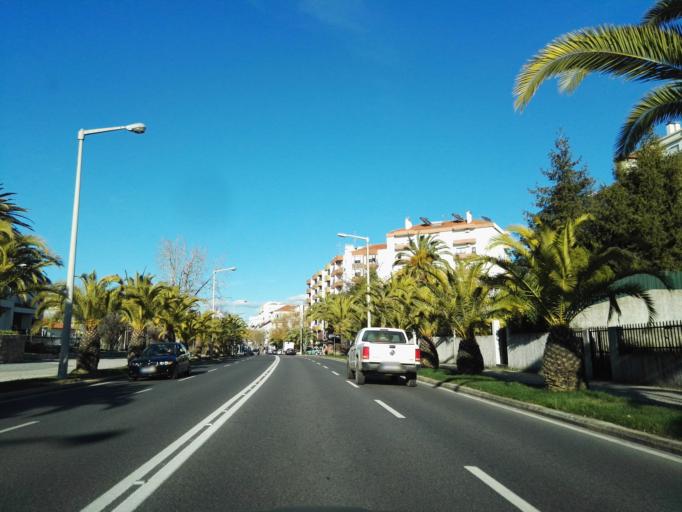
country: PT
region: Castelo Branco
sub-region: Castelo Branco
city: Castelo Branco
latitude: 39.8182
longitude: -7.4979
